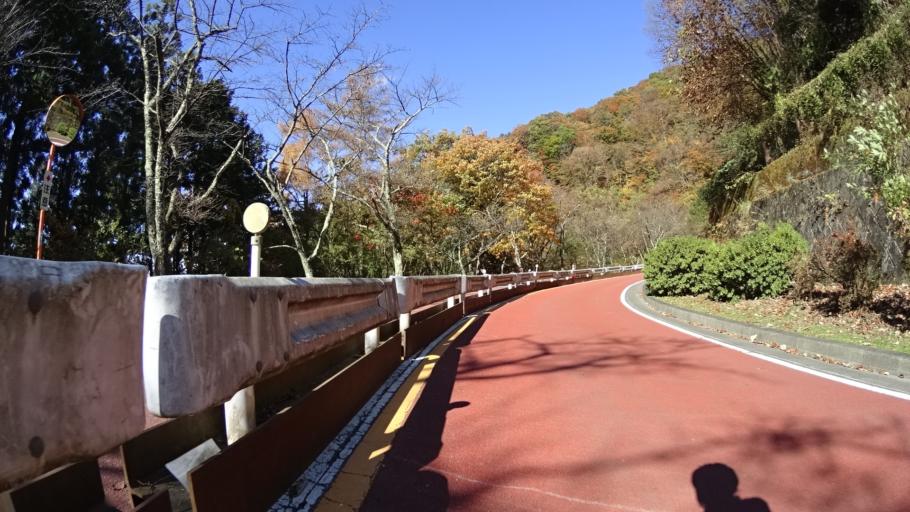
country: JP
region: Yamanashi
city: Uenohara
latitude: 35.7567
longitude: 139.0359
